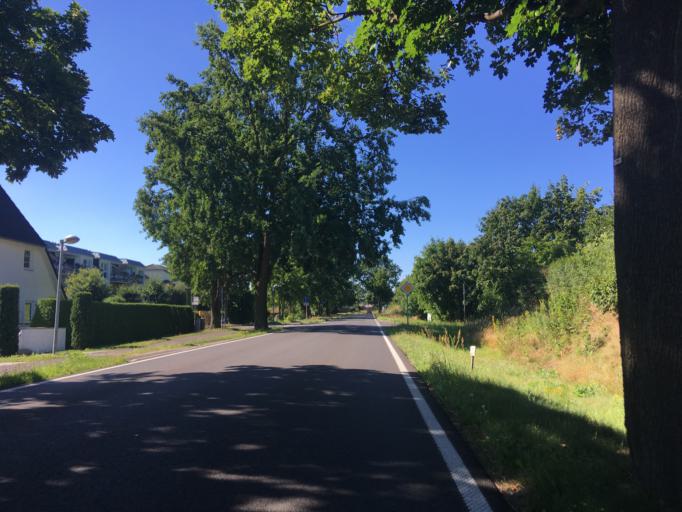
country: DE
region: Brandenburg
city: Altlandsberg
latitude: 52.5504
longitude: 13.7122
